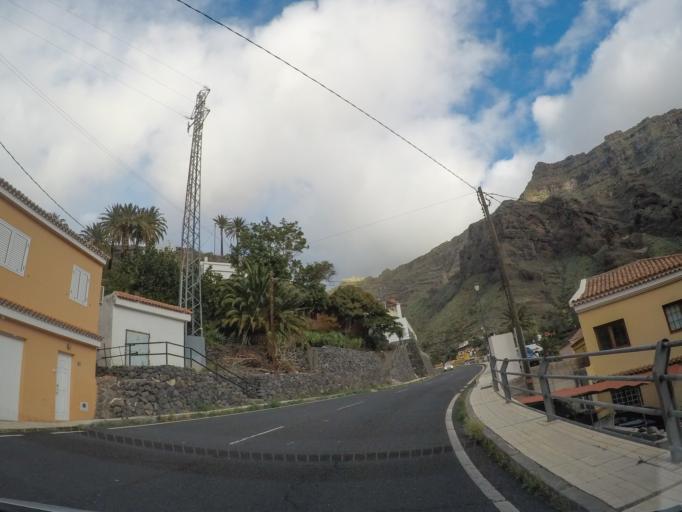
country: ES
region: Canary Islands
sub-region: Provincia de Santa Cruz de Tenerife
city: Vallehermosa
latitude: 28.1125
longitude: -17.3167
